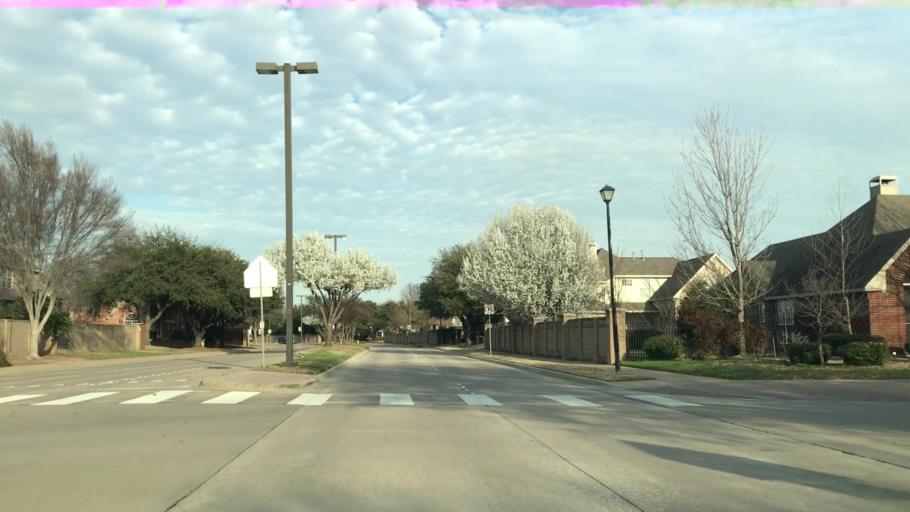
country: US
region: Texas
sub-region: Dallas County
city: Coppell
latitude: 32.9793
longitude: -97.0077
